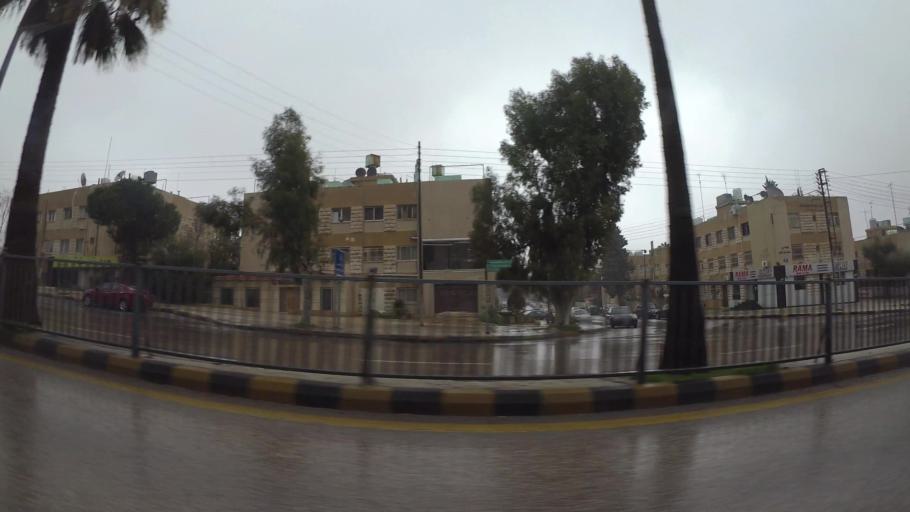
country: JO
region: Amman
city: Al Jubayhah
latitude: 31.9684
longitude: 35.8795
